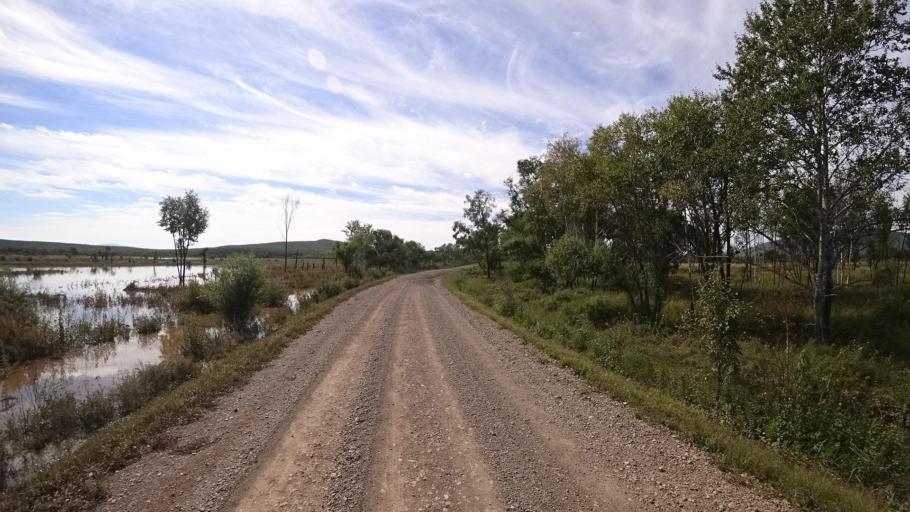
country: RU
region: Primorskiy
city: Kirovskiy
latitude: 44.7729
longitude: 133.6254
